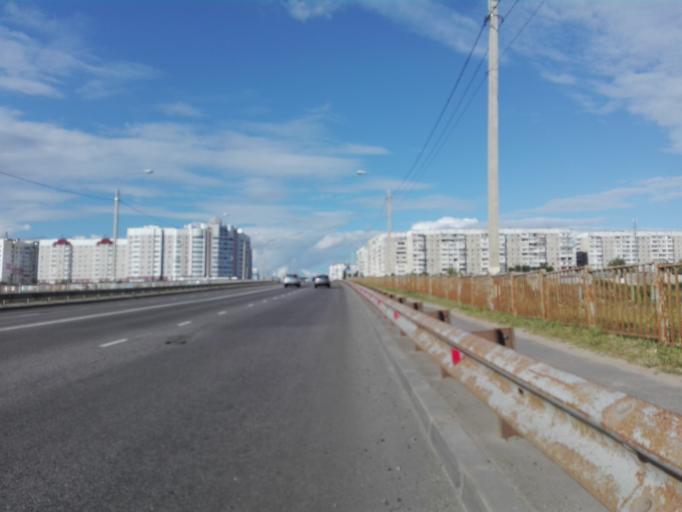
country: RU
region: Orjol
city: Orel
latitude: 53.0087
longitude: 36.1228
